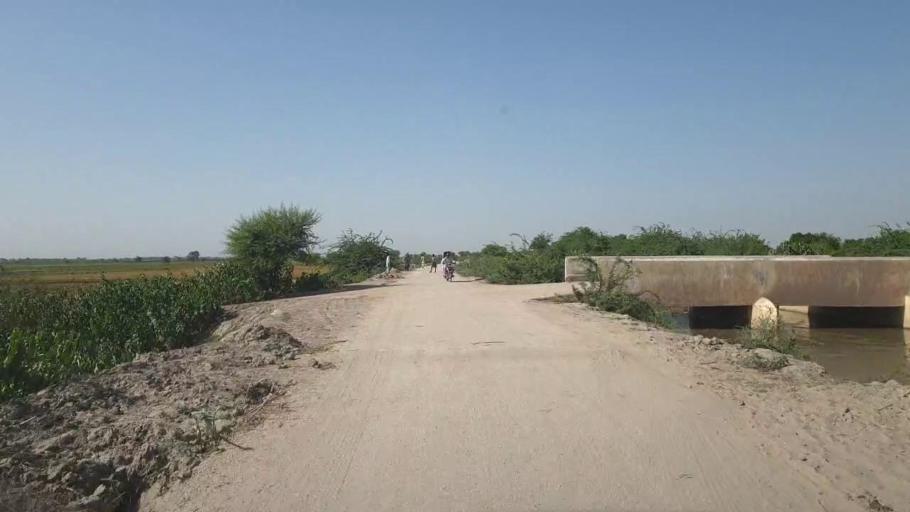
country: PK
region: Sindh
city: Kadhan
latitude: 24.5729
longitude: 68.9868
